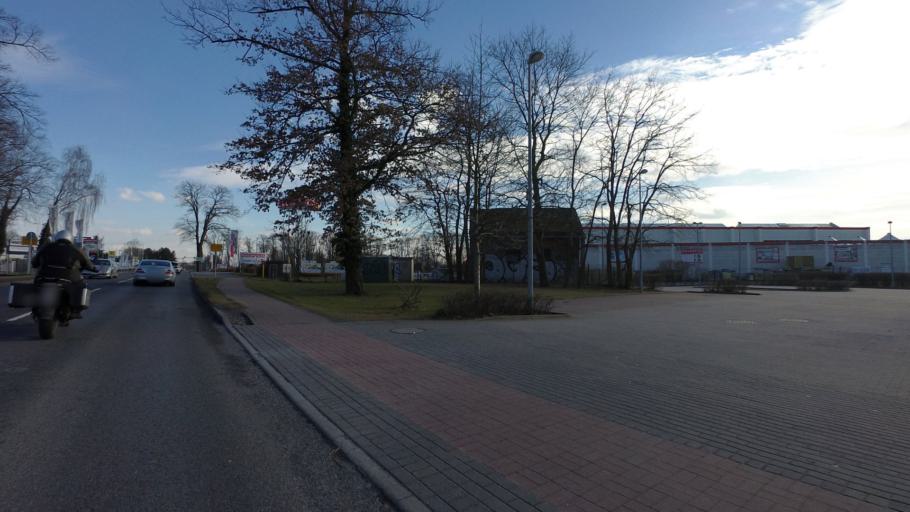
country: DE
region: Brandenburg
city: Birkenwerder
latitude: 52.7055
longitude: 13.2693
